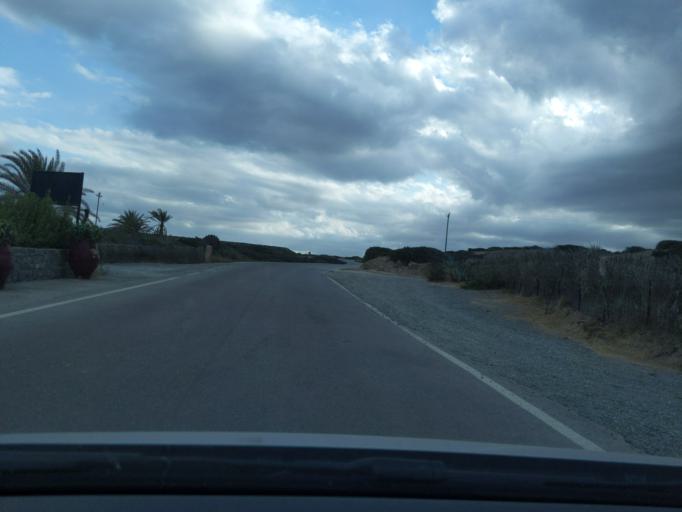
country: GR
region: Crete
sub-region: Nomos Lasithiou
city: Palekastro
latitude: 35.2499
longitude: 26.2511
